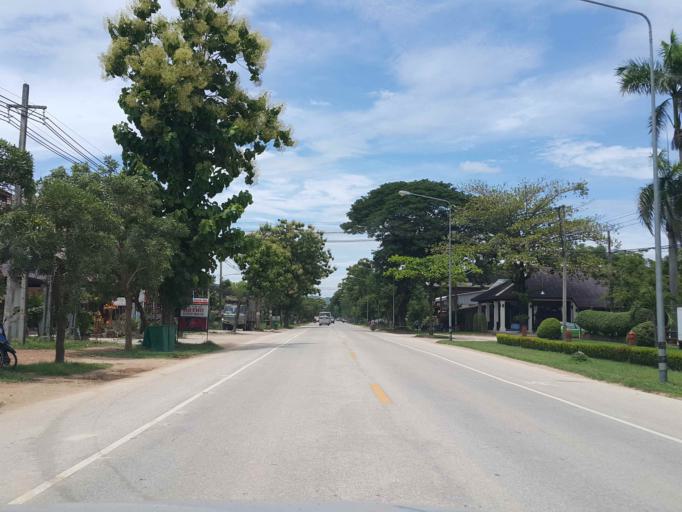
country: TH
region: Sukhothai
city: Ban Na
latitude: 17.0178
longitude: 99.7202
